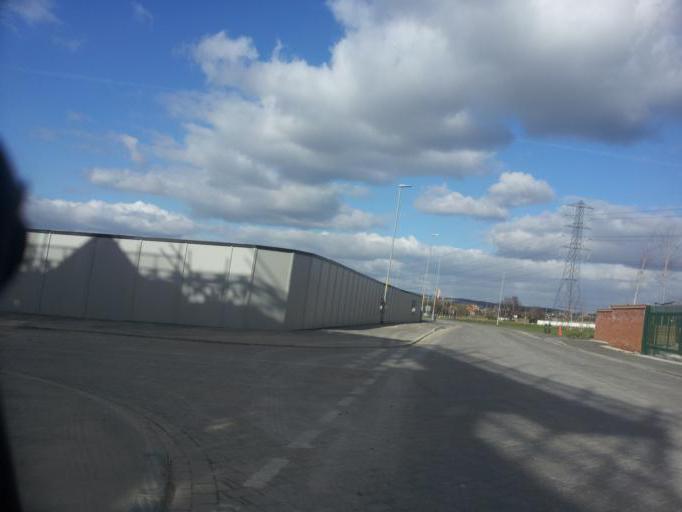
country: GB
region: England
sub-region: Medway
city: Halling
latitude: 51.3400
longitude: 0.4580
